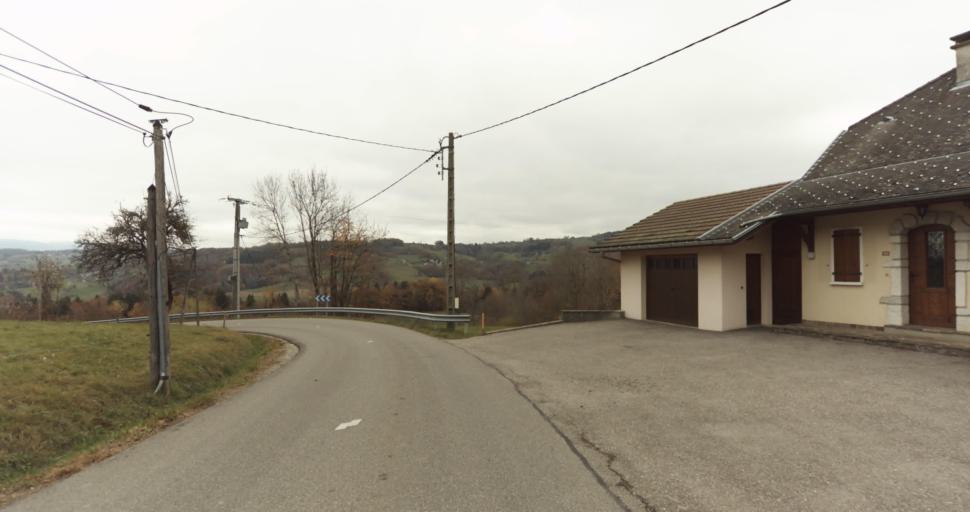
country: FR
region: Rhone-Alpes
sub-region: Departement de la Haute-Savoie
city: Thorens-Glieres
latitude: 45.9896
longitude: 6.2194
